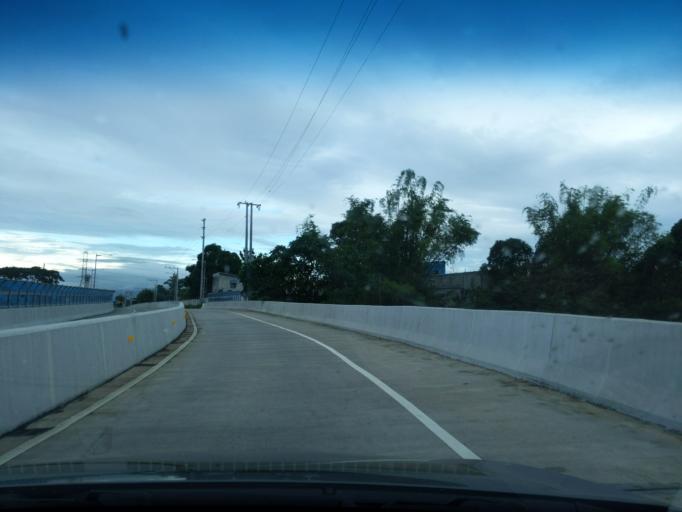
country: PH
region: Calabarzon
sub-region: Province of Cavite
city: Puting Kahoy
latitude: 14.2305
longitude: 121.0475
